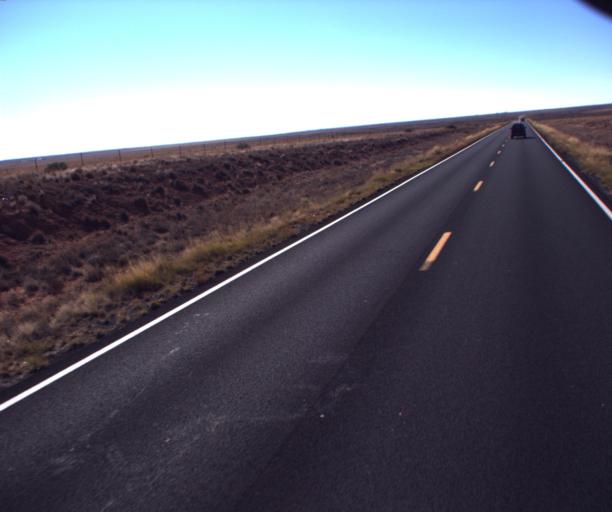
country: US
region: Arizona
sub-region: Navajo County
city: Dilkon
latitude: 35.2638
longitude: -110.4295
